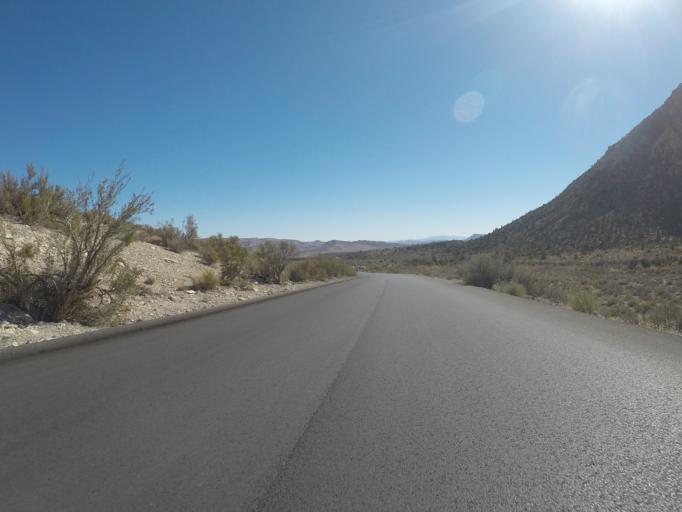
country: US
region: Nevada
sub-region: Clark County
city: Summerlin South
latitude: 36.1520
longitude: -115.4859
